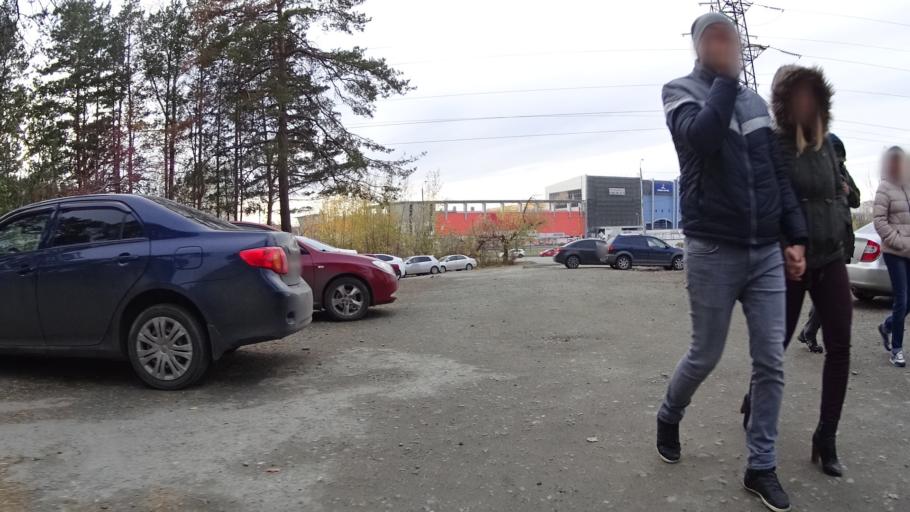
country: RU
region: Chelyabinsk
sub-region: Gorod Chelyabinsk
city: Chelyabinsk
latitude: 55.1693
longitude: 61.3595
